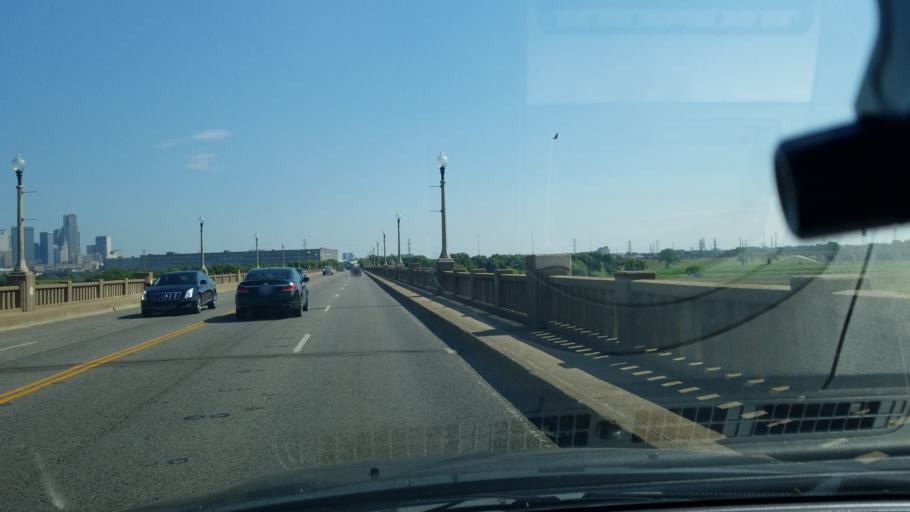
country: US
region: Texas
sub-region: Dallas County
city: Dallas
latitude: 32.7522
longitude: -96.7976
